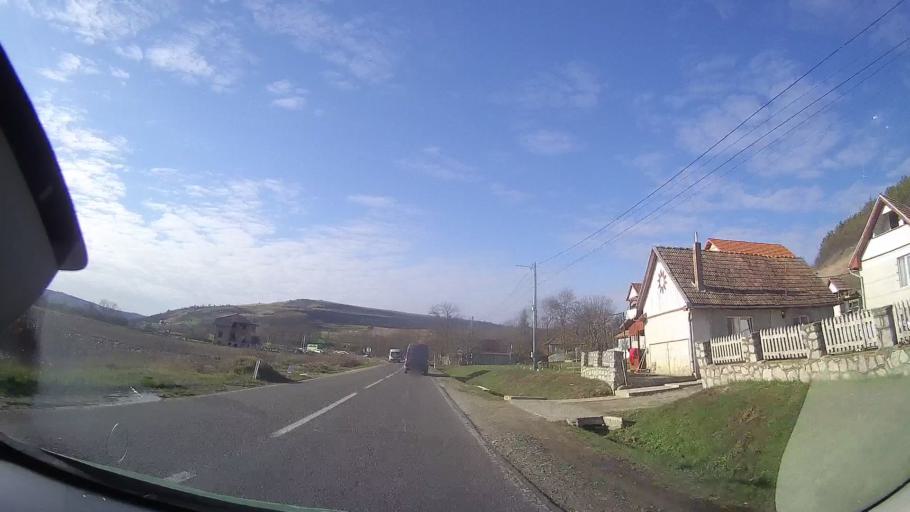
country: RO
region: Cluj
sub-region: Comuna Caianu
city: Caianu
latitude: 46.8019
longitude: 23.9323
